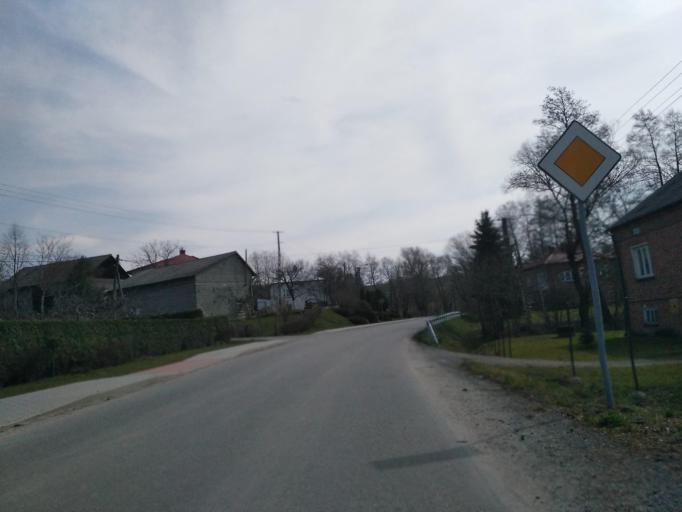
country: PL
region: Subcarpathian Voivodeship
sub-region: Powiat ropczycko-sedziszowski
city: Iwierzyce
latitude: 50.0195
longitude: 21.7924
